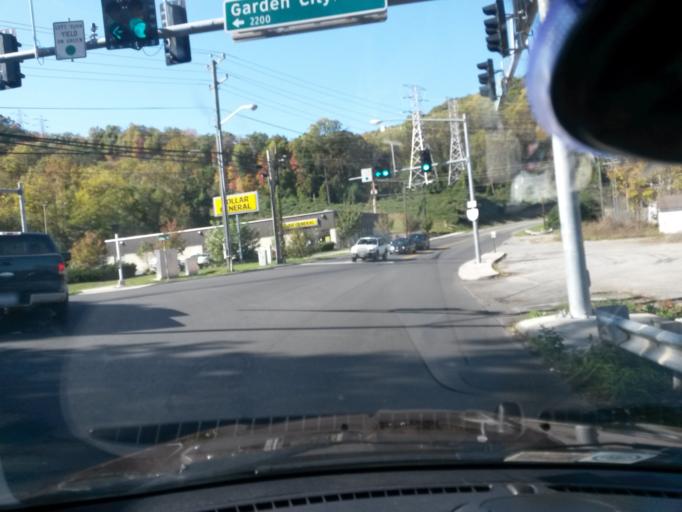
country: US
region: Virginia
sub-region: City of Roanoke
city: Cedar Bluff
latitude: 37.2495
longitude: -79.9195
